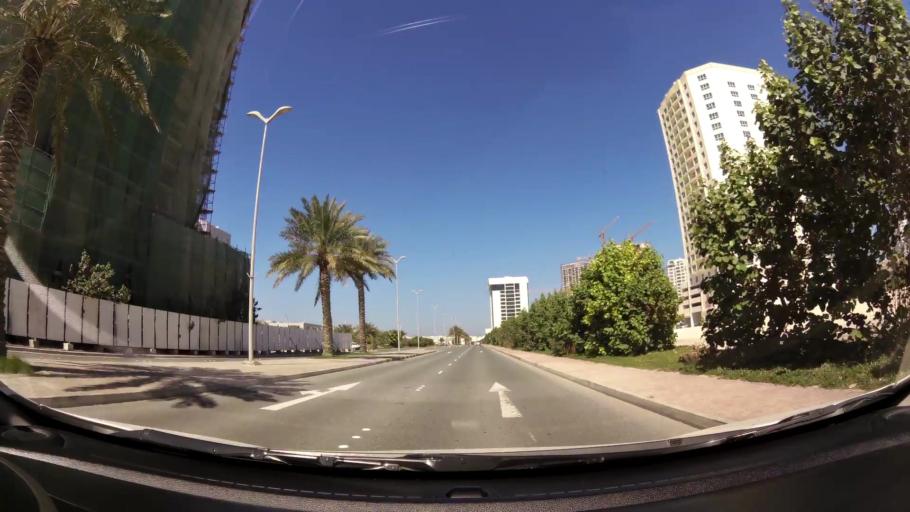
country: BH
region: Muharraq
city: Al Hadd
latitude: 26.2880
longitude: 50.6604
